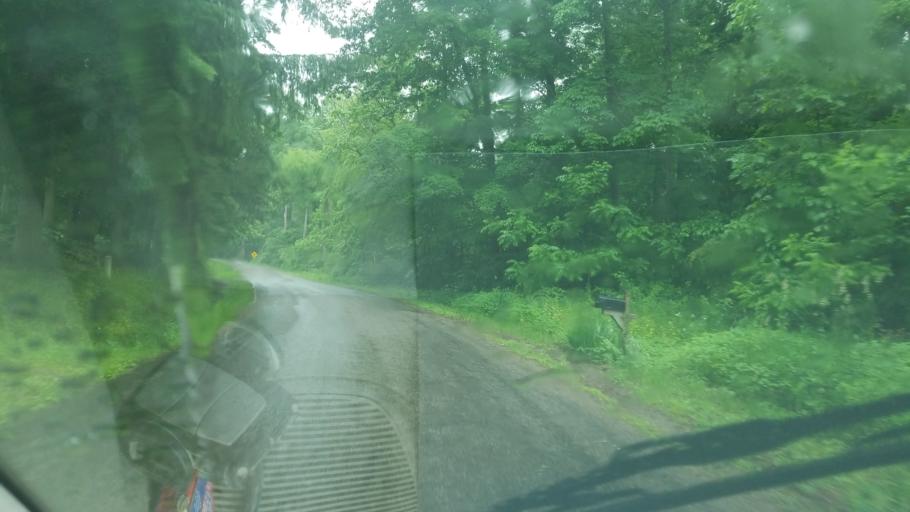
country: US
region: Ohio
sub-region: Sandusky County
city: Bellville
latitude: 40.6262
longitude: -82.4296
